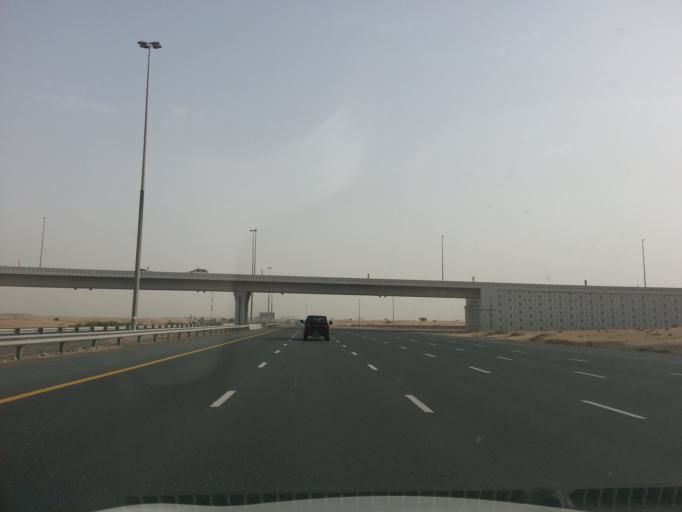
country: AE
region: Dubai
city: Dubai
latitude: 24.9784
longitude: 55.2406
